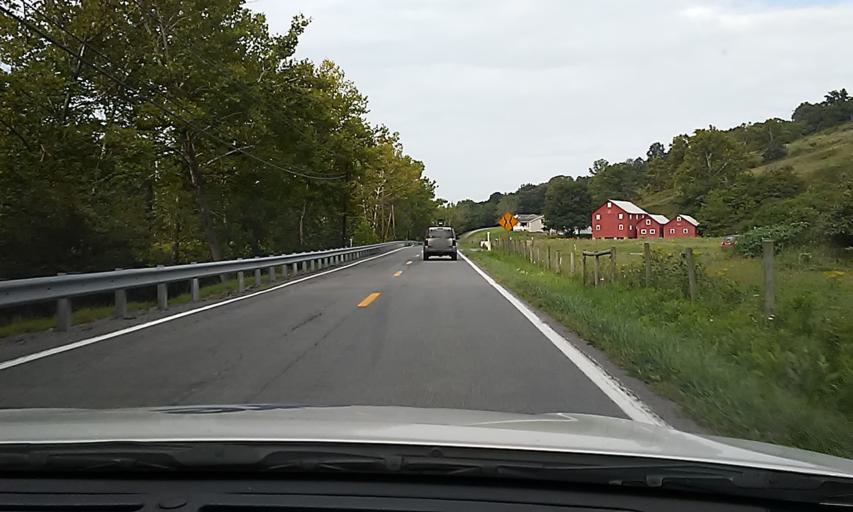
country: US
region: West Virginia
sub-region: Marion County
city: Mannington
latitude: 39.6906
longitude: -80.3188
